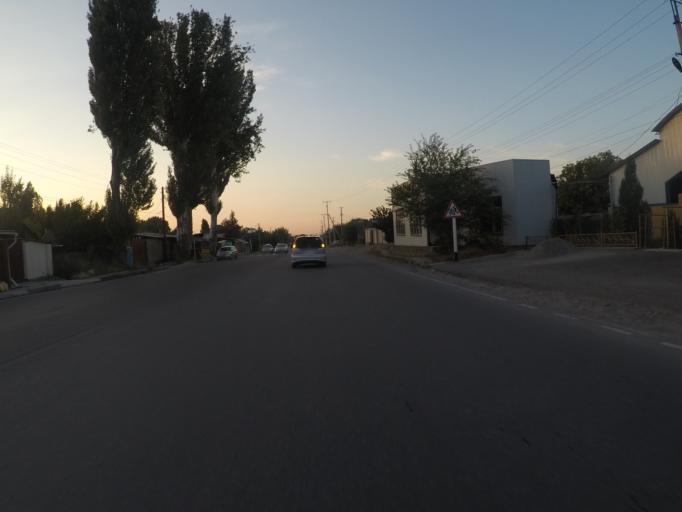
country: KG
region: Chuy
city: Lebedinovka
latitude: 42.8095
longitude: 74.6465
